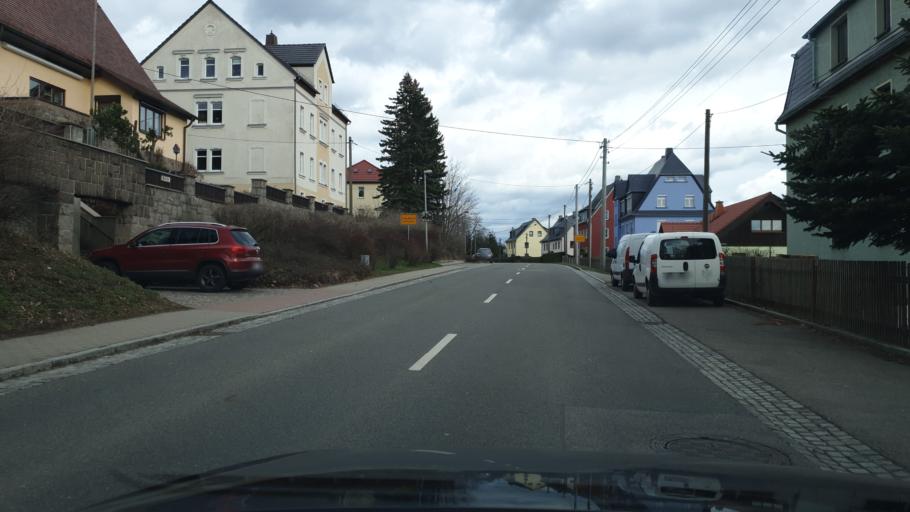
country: DE
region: Saxony
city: Claussnitz
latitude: 50.9318
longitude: 12.8749
